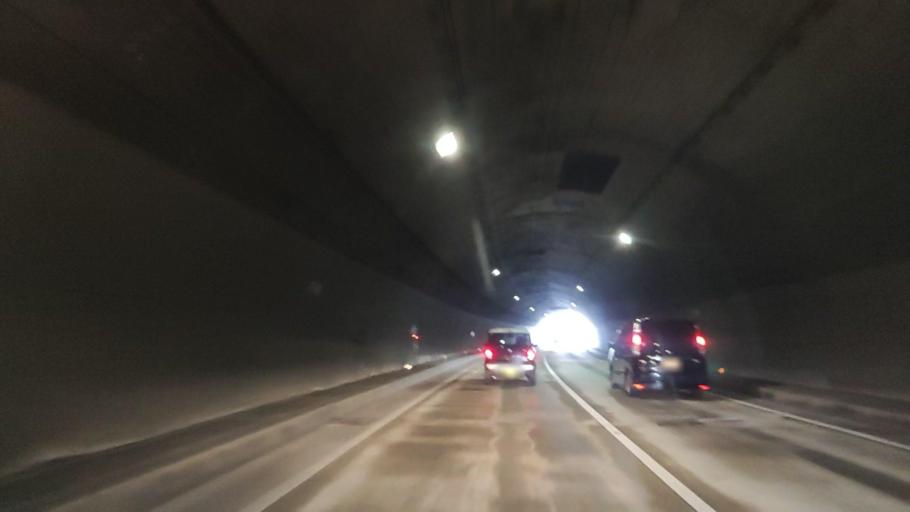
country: JP
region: Hiroshima
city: Onomichi
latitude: 34.4470
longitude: 133.2294
